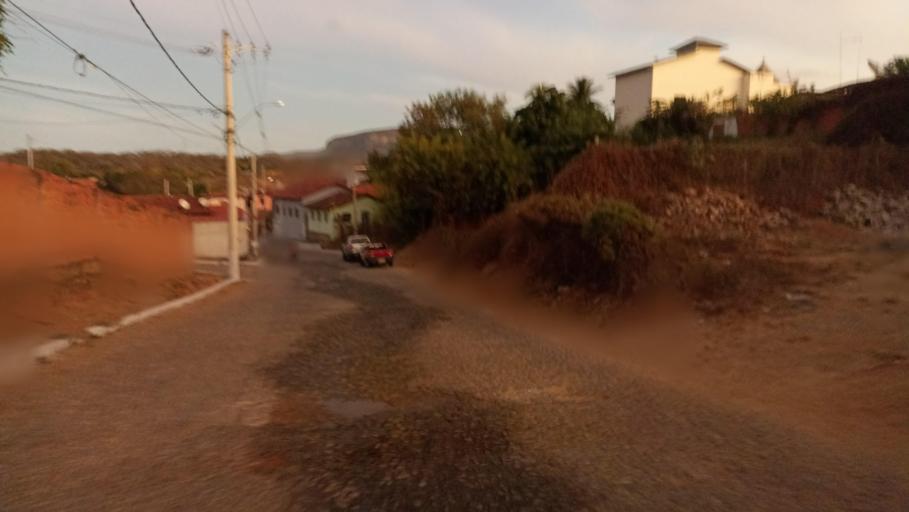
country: BR
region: Minas Gerais
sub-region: Aracuai
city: Aracuai
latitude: -16.6176
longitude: -42.1811
